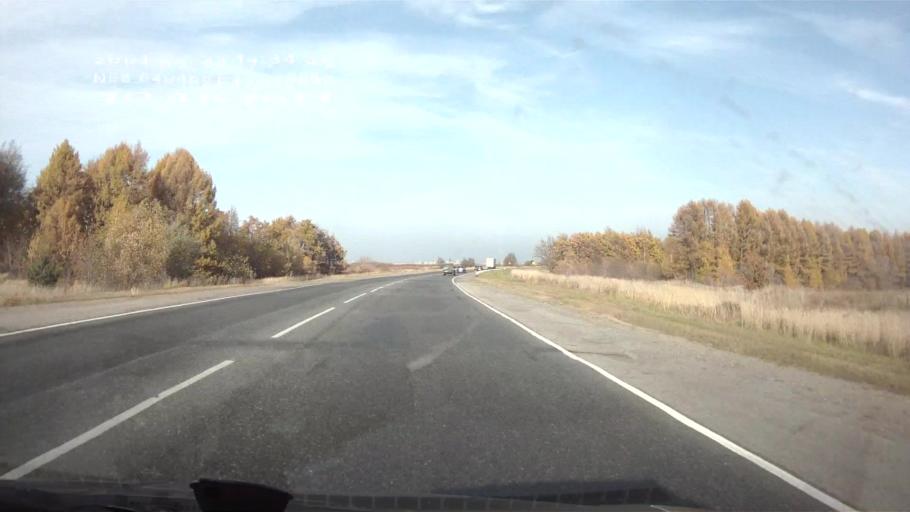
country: RU
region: Chuvashia
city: Kugesi
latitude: 56.0490
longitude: 47.3722
